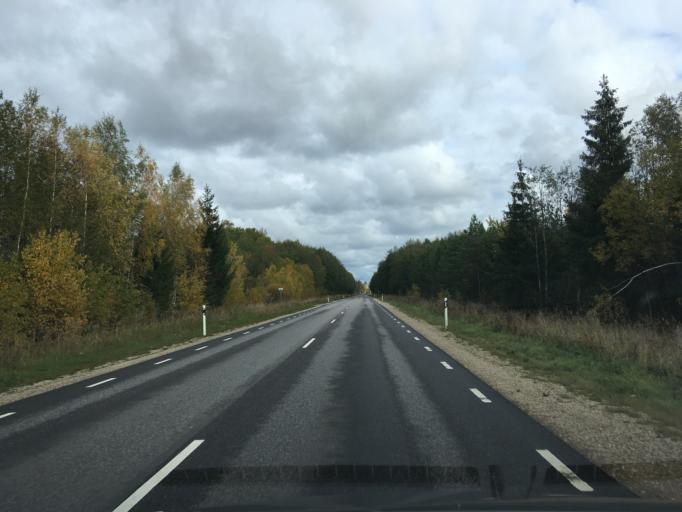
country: EE
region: Harju
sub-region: Anija vald
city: Kehra
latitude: 59.2389
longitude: 25.2921
